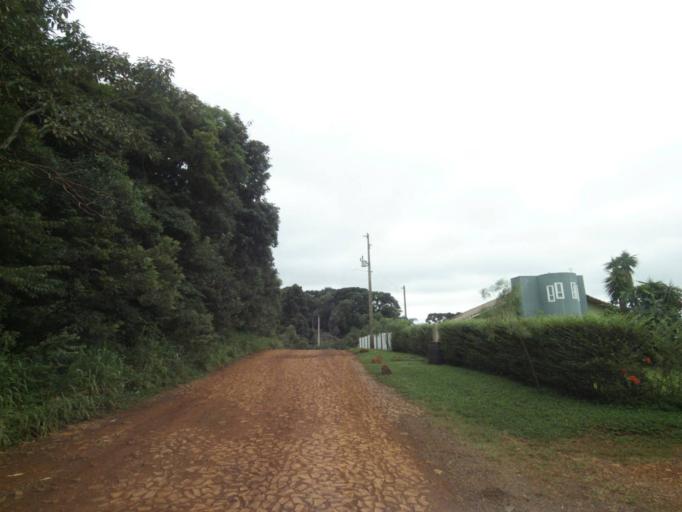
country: BR
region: Parana
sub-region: Pitanga
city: Pitanga
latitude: -24.9275
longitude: -51.8714
